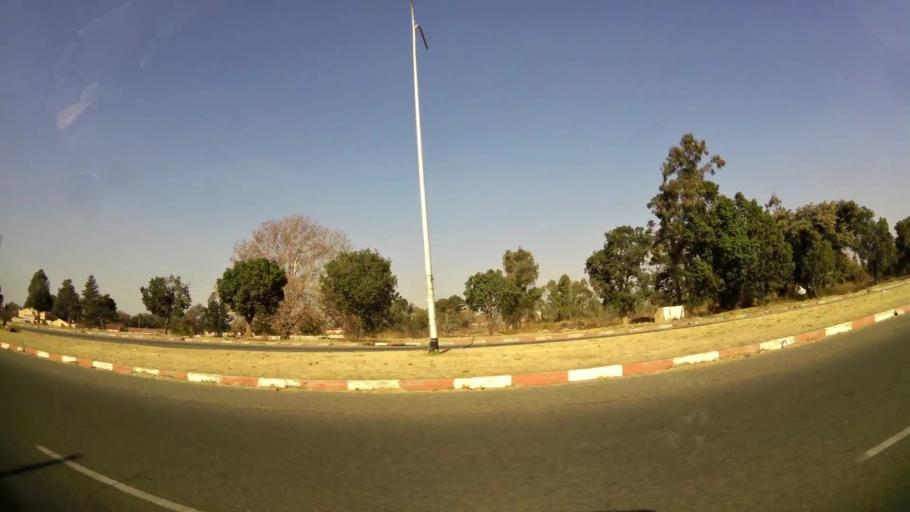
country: ZA
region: Gauteng
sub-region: West Rand District Municipality
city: Randfontein
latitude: -26.1581
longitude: 27.7172
